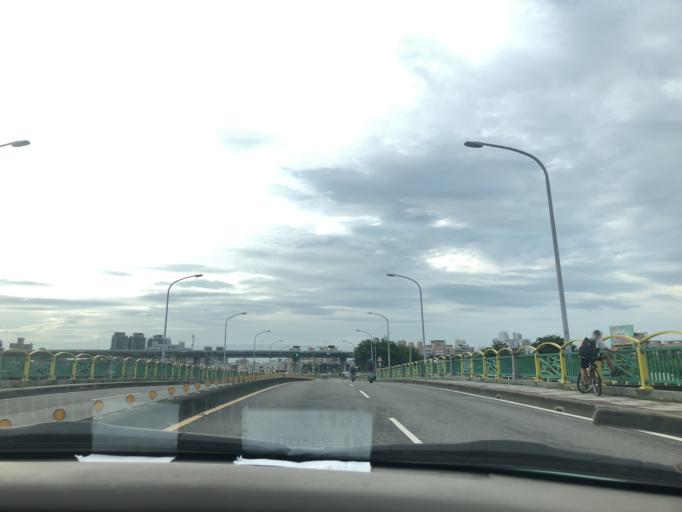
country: TW
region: Taiwan
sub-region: Taichung City
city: Taichung
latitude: 24.0976
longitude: 120.6950
